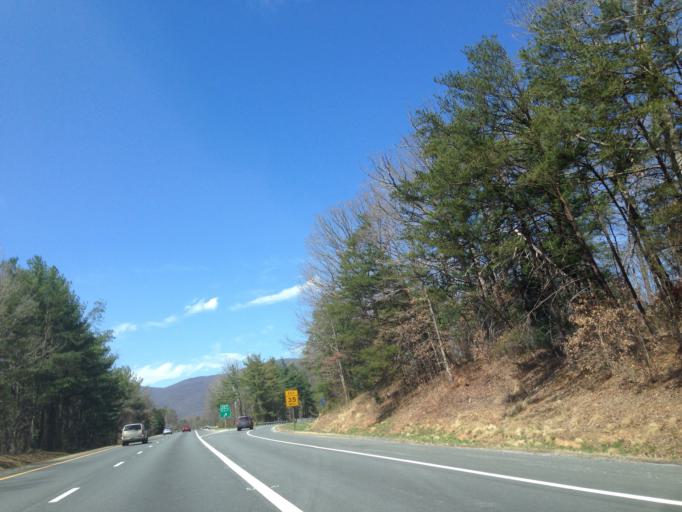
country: US
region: Virginia
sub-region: Albemarle County
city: Crozet
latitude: 38.0429
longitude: -78.7217
